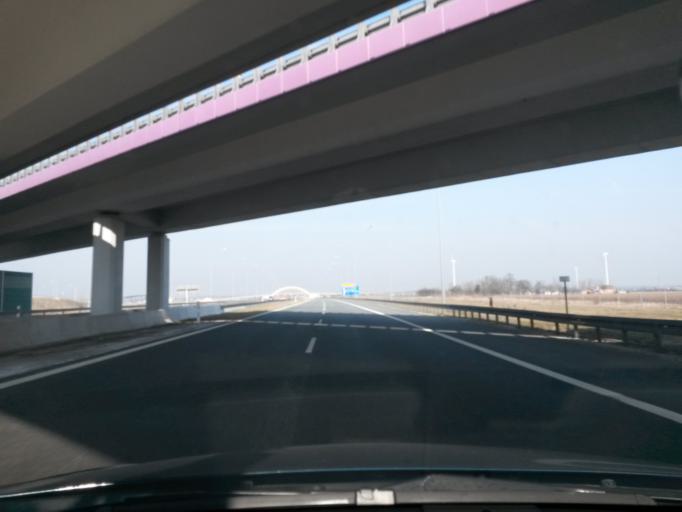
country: PL
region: Lodz Voivodeship
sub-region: Powiat kutnowski
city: Krzyzanow
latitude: 52.2188
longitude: 19.4730
